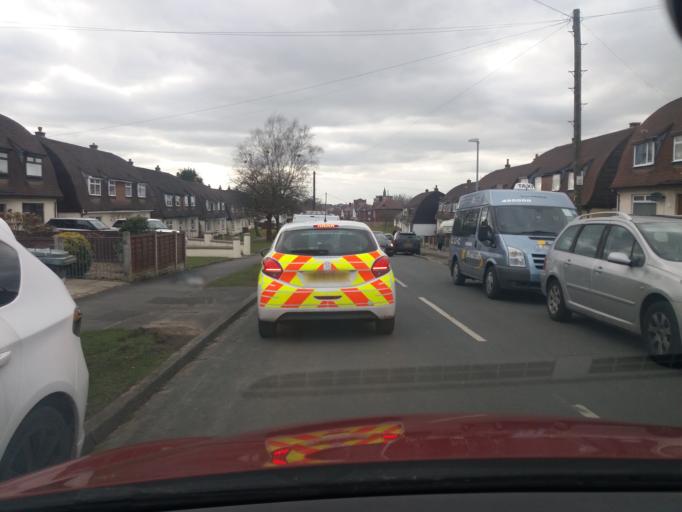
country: GB
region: England
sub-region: Lancashire
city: Chorley
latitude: 53.6546
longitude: -2.6211
